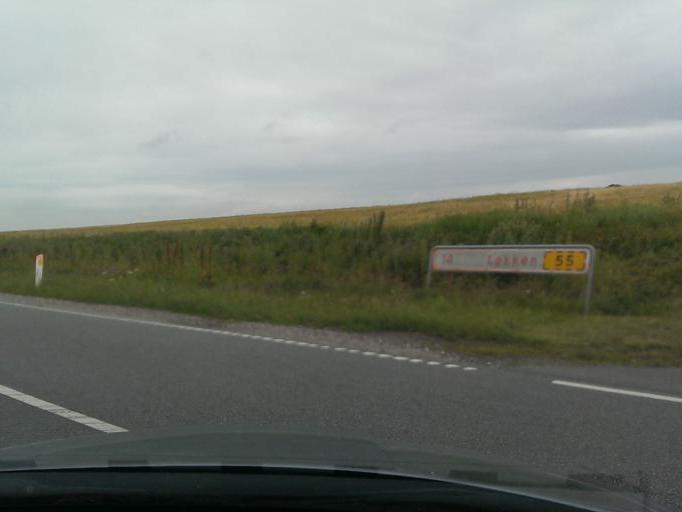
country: DK
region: North Denmark
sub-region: Hjorring Kommune
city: Vra
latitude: 57.3574
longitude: 9.9251
